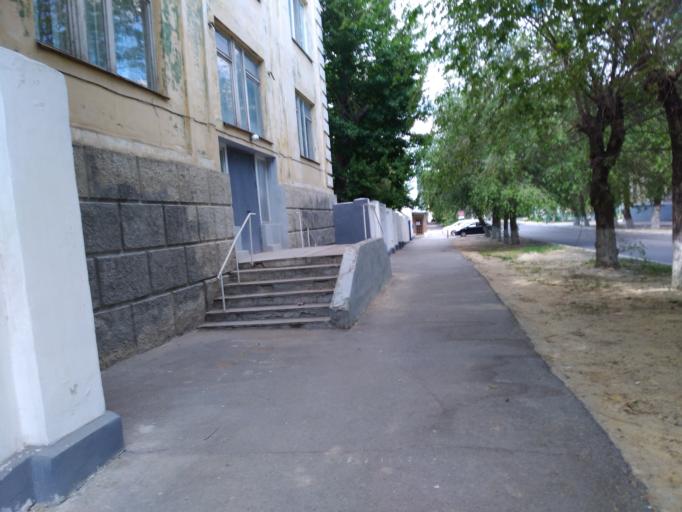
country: RU
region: Volgograd
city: Volgograd
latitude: 48.7194
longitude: 44.5353
